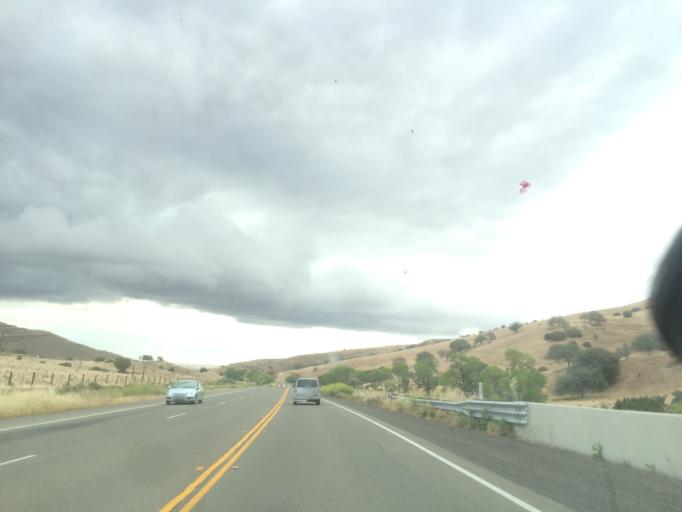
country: US
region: California
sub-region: San Luis Obispo County
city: Shandon
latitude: 35.7726
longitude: -120.1724
